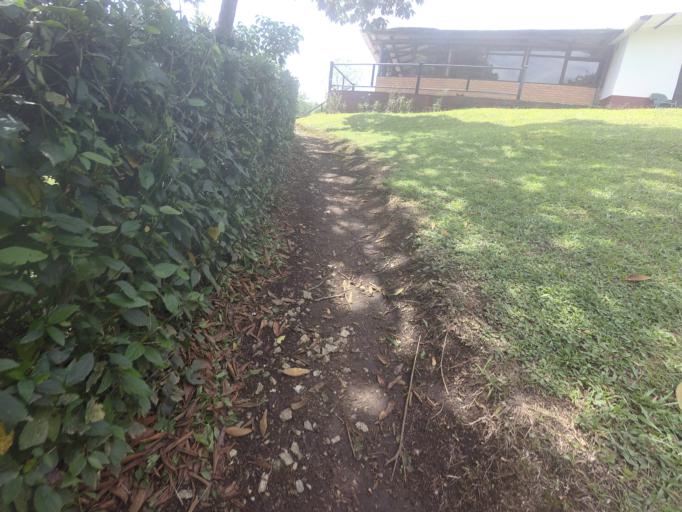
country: CO
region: Huila
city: San Agustin
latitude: 1.8896
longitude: -76.2969
